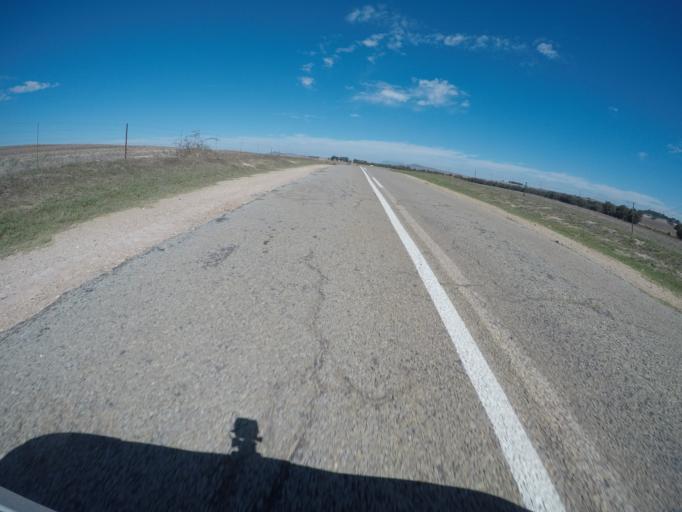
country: ZA
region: Western Cape
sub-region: City of Cape Town
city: Atlantis
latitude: -33.6009
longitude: 18.6414
